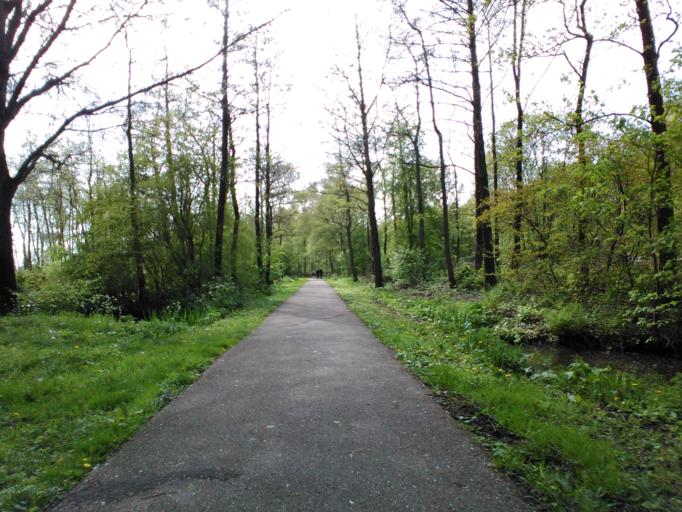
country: NL
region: South Holland
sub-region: Bodegraven-Reeuwijk
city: Bodegraven
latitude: 52.0642
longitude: 4.7423
